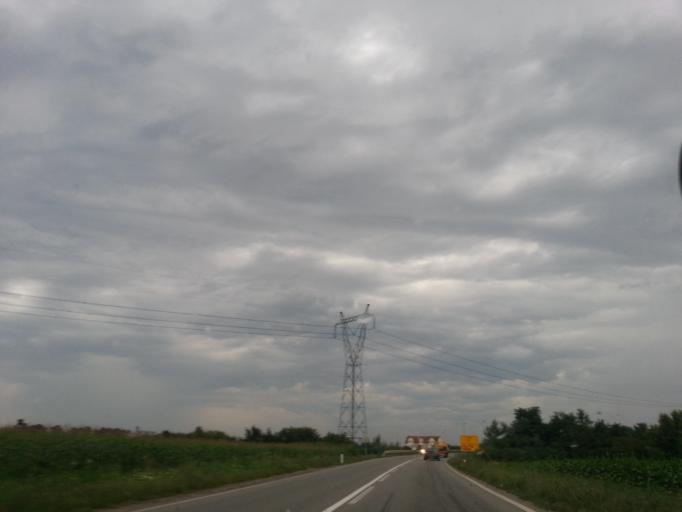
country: BA
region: Republika Srpska
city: Velika Obarska
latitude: 44.7692
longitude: 19.1751
